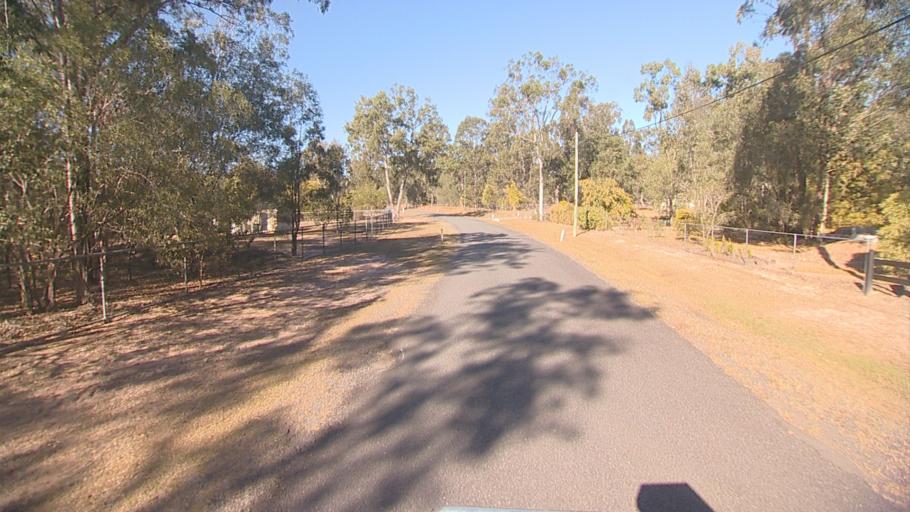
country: AU
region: Queensland
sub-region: Logan
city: North Maclean
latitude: -27.8101
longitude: 152.9711
